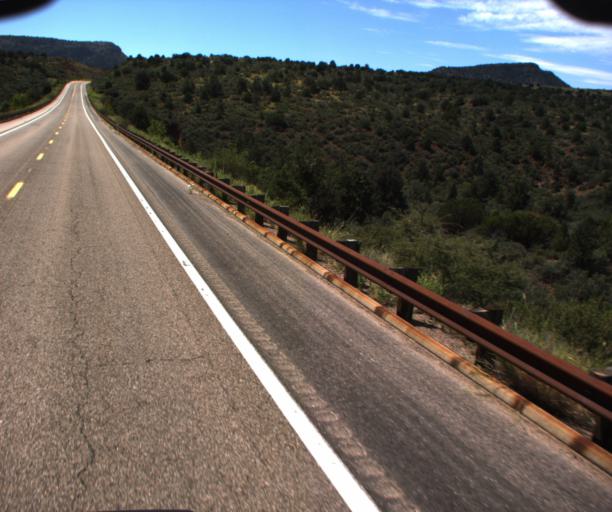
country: US
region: Arizona
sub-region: Gila County
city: Globe
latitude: 33.5391
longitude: -110.6928
